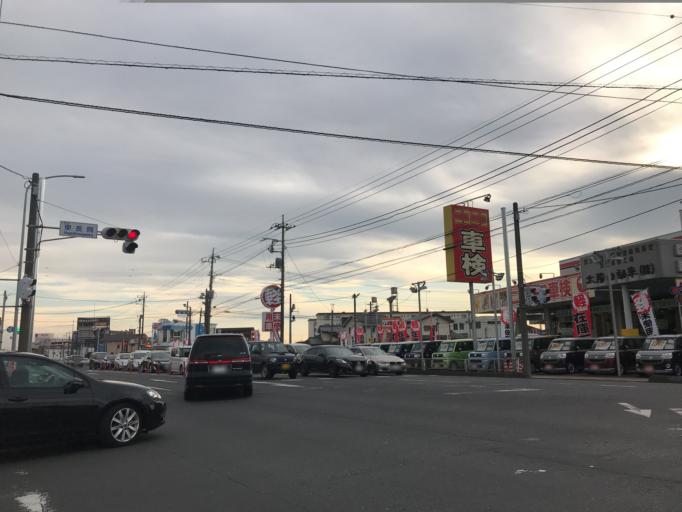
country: JP
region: Gunma
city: Ota
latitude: 36.3005
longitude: 139.3992
